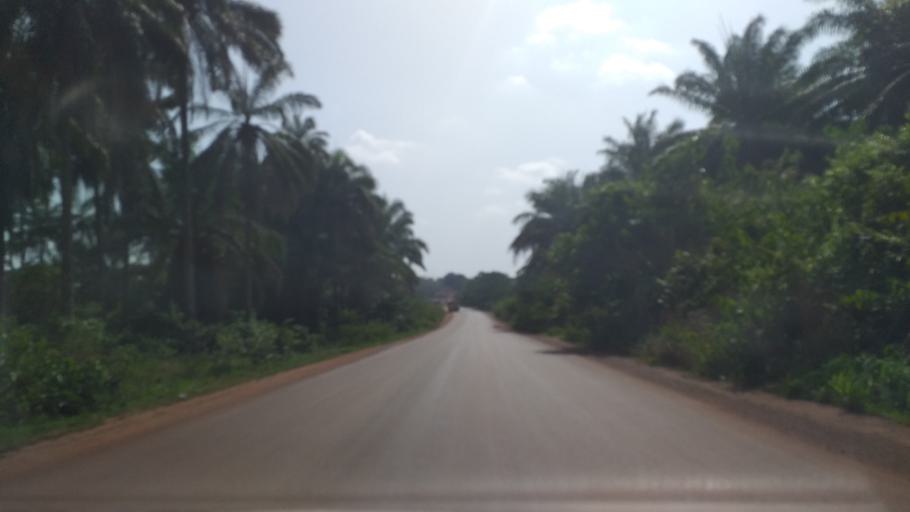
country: GN
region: Boke
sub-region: Boke Prefecture
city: Boke
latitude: 10.8345
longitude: -14.3606
